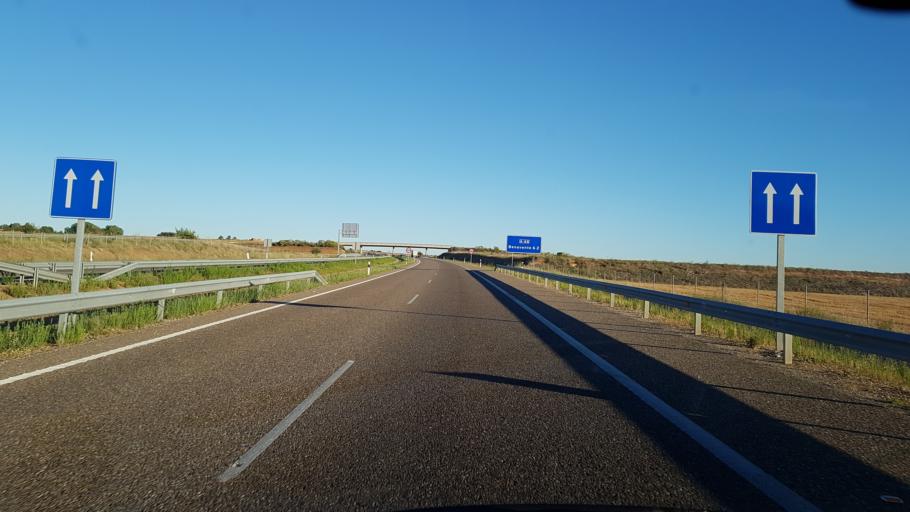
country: ES
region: Castille and Leon
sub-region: Provincia de Zamora
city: Monfarracinos
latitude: 41.5481
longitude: -5.7172
